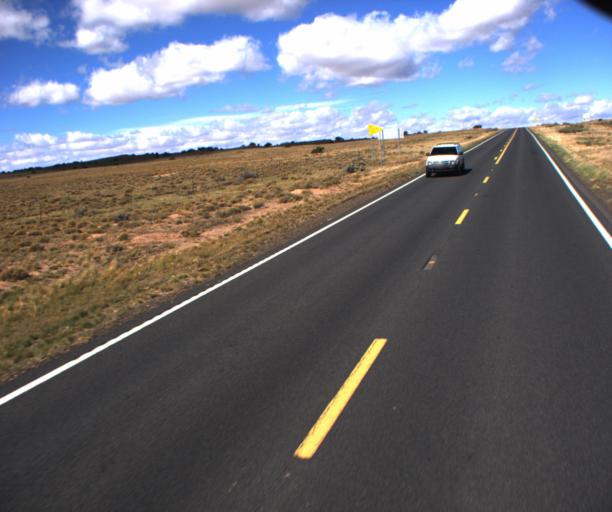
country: US
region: Arizona
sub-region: Apache County
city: Houck
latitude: 35.0311
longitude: -109.2548
